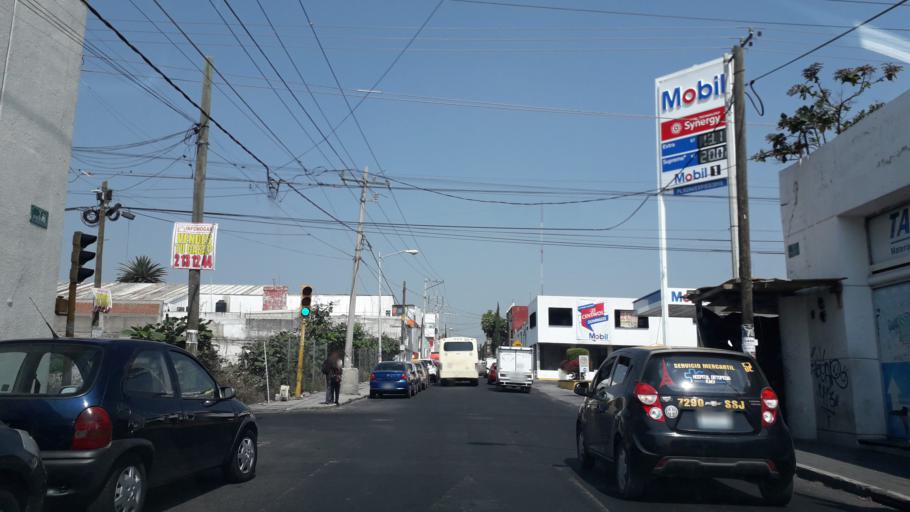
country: MX
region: Puebla
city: Puebla
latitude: 19.0521
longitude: -98.2114
